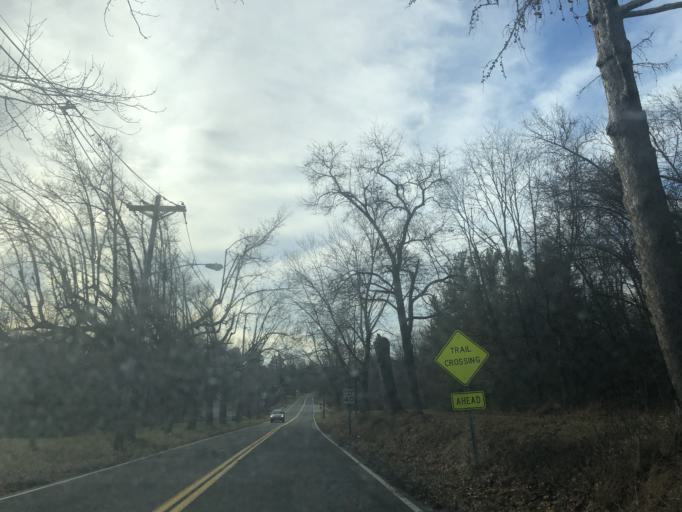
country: US
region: New Jersey
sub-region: Somerset County
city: Kingston
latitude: 40.3719
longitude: -74.6152
